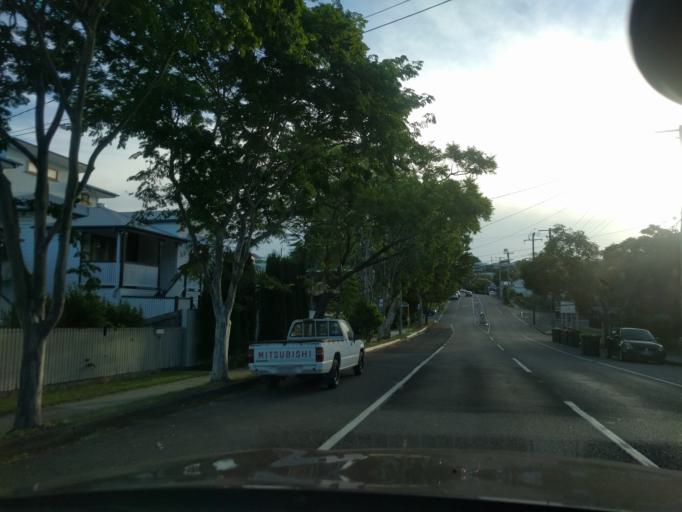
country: AU
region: Queensland
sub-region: Brisbane
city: Milton
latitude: -27.4696
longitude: 152.9973
